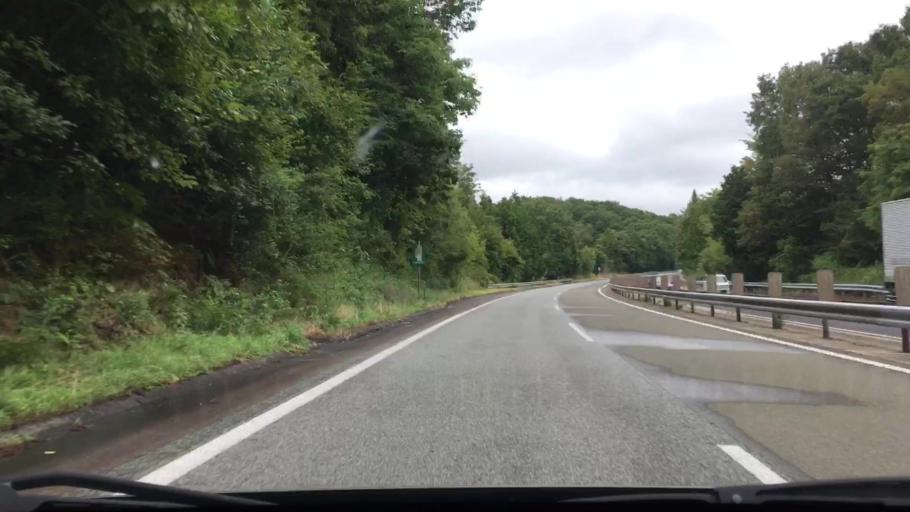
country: JP
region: Hiroshima
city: Miyoshi
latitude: 34.7900
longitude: 132.8803
